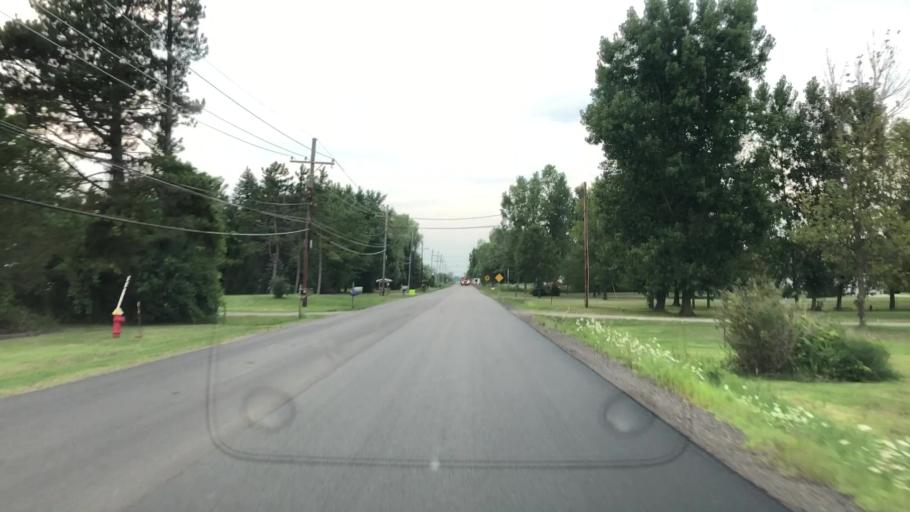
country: US
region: New York
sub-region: Erie County
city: Elma Center
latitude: 42.8193
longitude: -78.6059
